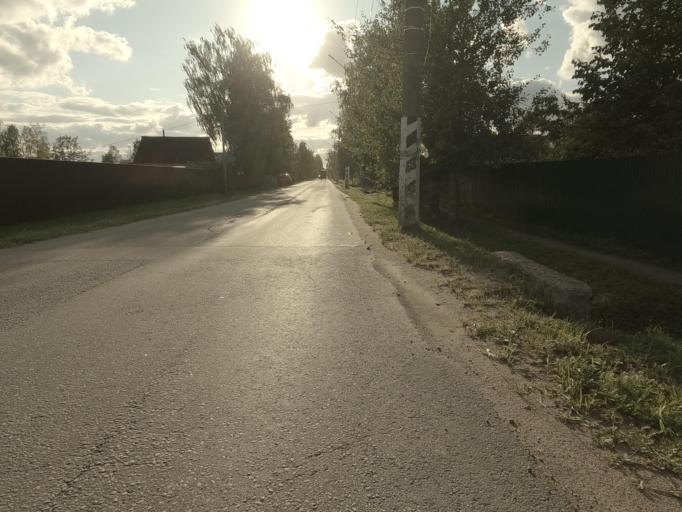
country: RU
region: Leningrad
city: Mga
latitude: 59.7573
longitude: 31.0767
